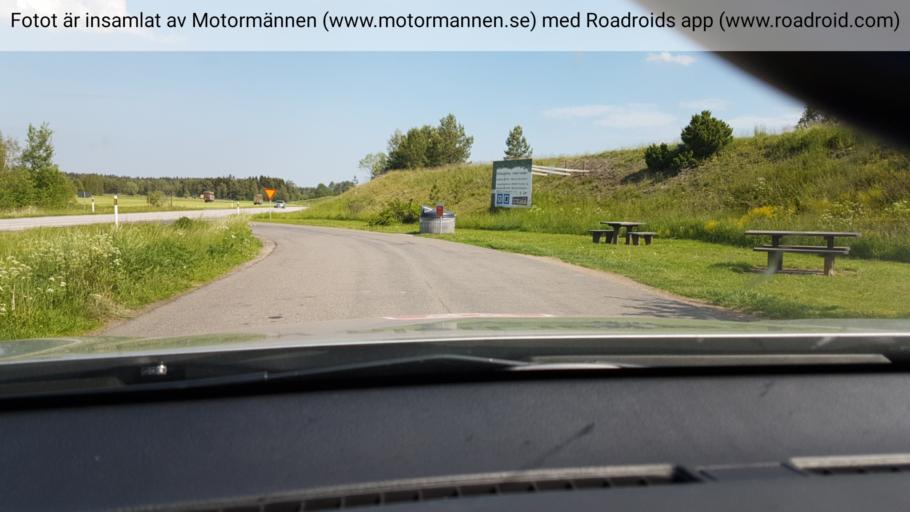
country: SE
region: Vaestra Goetaland
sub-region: Falkopings Kommun
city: Falkoeping
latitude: 57.9932
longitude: 13.5487
